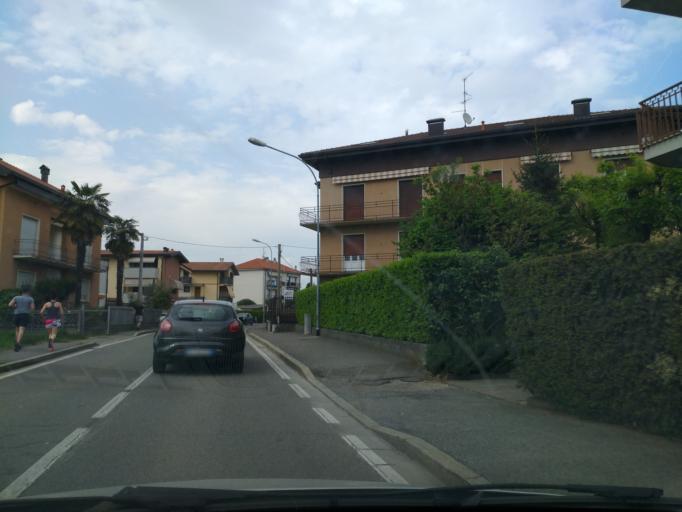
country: IT
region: Lombardy
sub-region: Provincia di Como
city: Cantu
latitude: 45.7271
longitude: 9.1515
